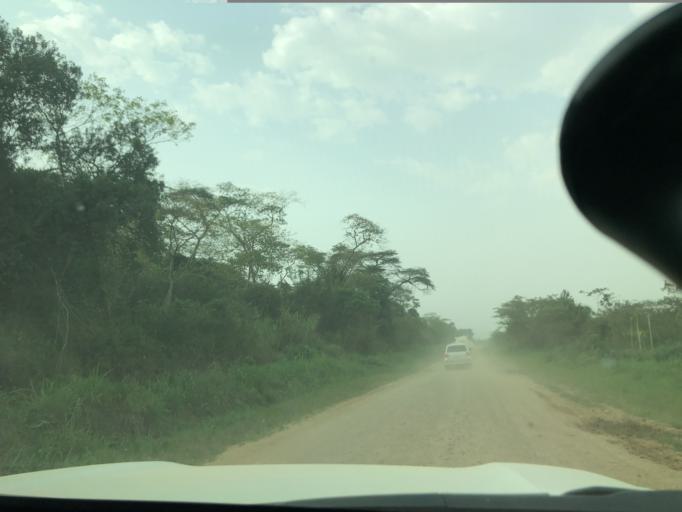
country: UG
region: Western Region
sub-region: Kasese District
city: Margherita
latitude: 0.2396
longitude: 29.6785
